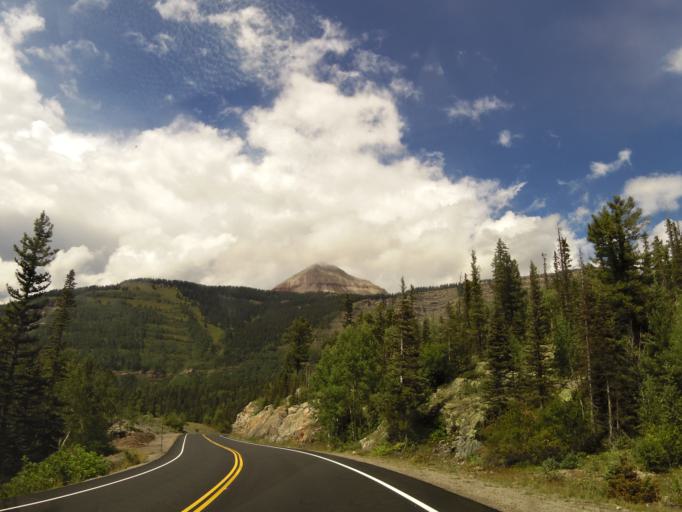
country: US
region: Colorado
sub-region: San Juan County
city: Silverton
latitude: 37.6773
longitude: -107.7824
